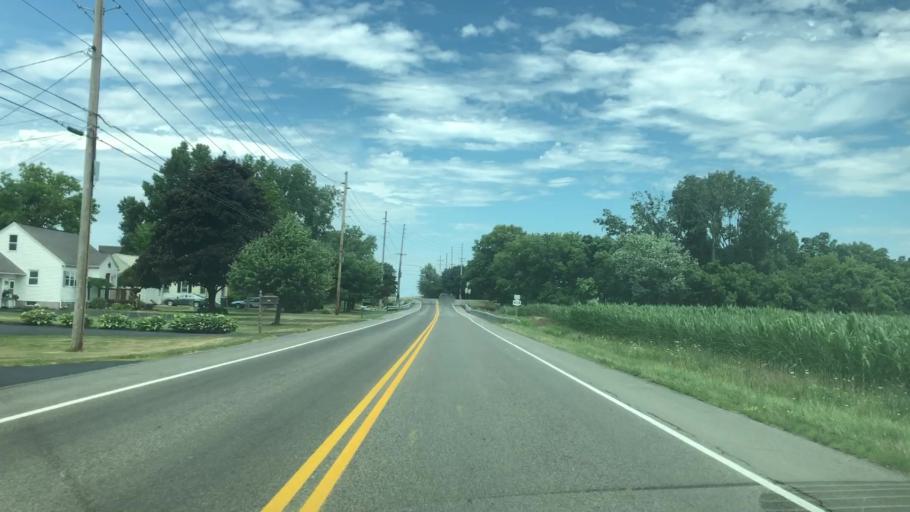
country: US
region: New York
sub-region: Monroe County
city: Webster
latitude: 43.2163
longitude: -77.4001
